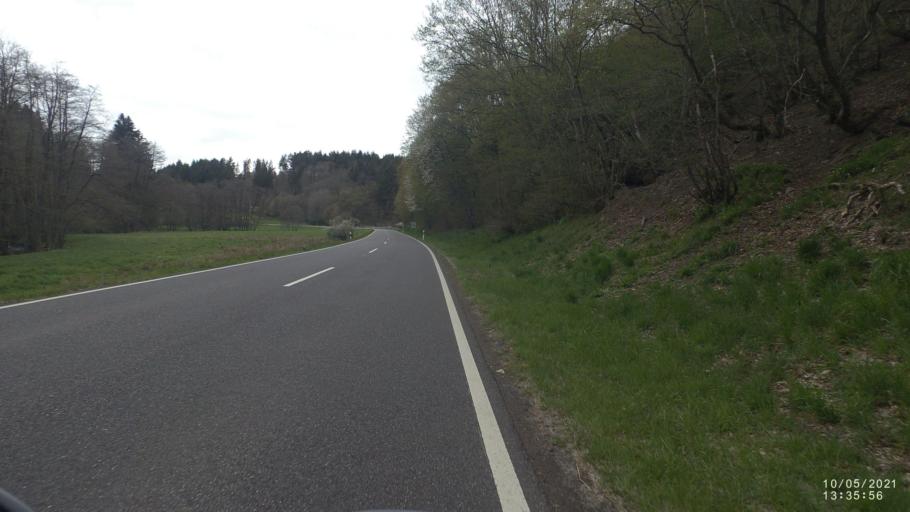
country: DE
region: Rheinland-Pfalz
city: Virneburg
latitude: 50.3369
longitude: 7.0698
